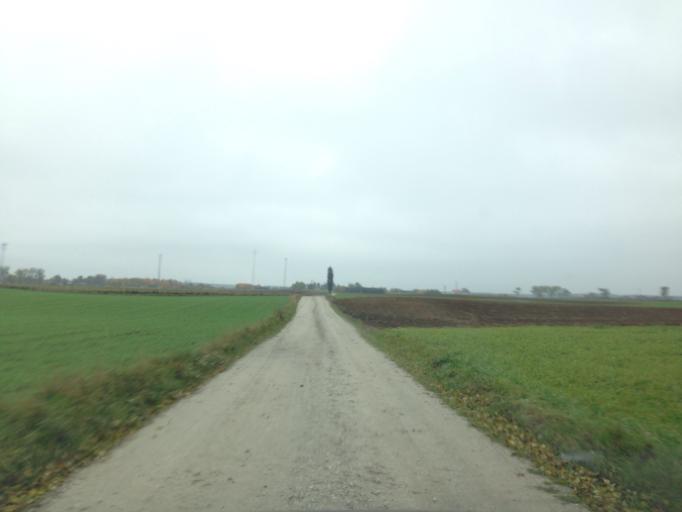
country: PL
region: Kujawsko-Pomorskie
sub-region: Powiat brodnicki
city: Gorzno
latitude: 53.2040
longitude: 19.6200
